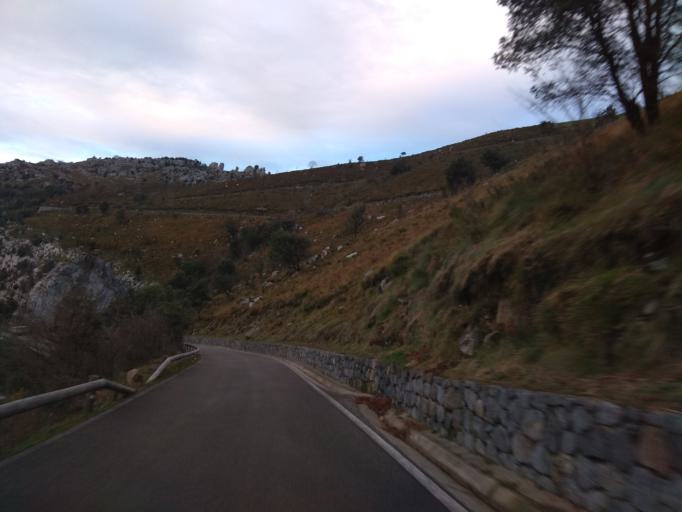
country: ES
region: Cantabria
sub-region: Provincia de Cantabria
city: Arredondo
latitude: 43.2031
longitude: -3.5851
